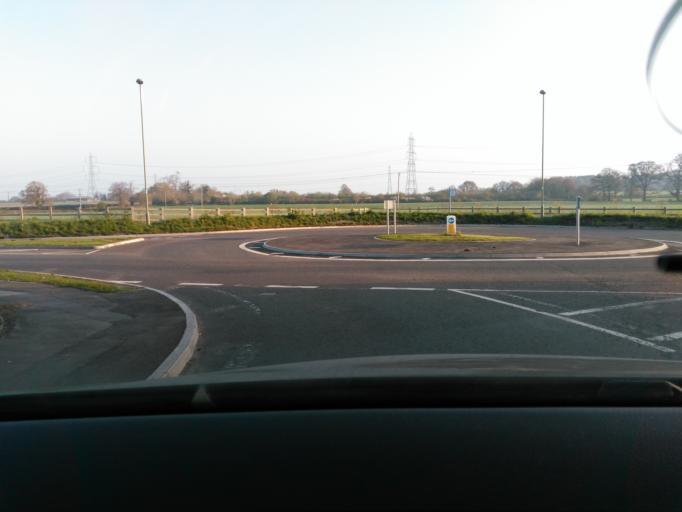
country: GB
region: England
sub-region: West Berkshire
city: Stratfield Mortimer
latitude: 51.3251
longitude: -1.0445
